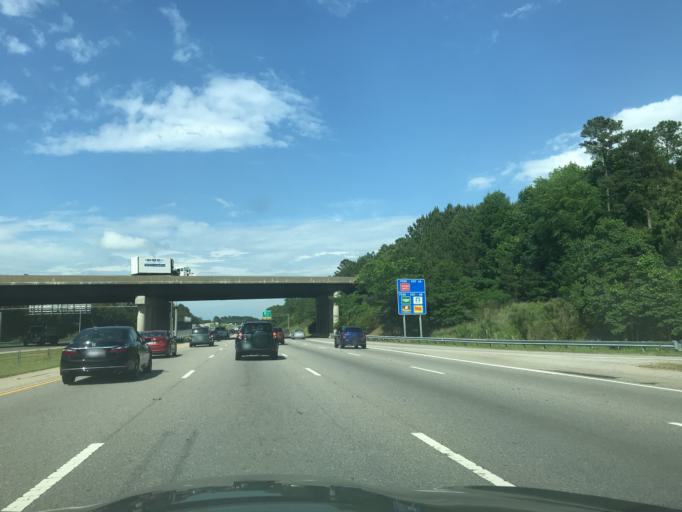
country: US
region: North Carolina
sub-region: Wake County
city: Morrisville
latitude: 35.8980
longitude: -78.7853
